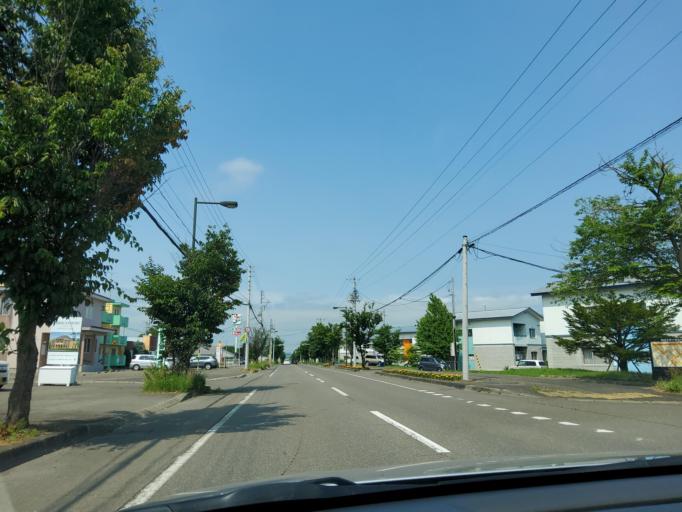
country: JP
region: Hokkaido
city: Obihiro
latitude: 42.9020
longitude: 143.0488
